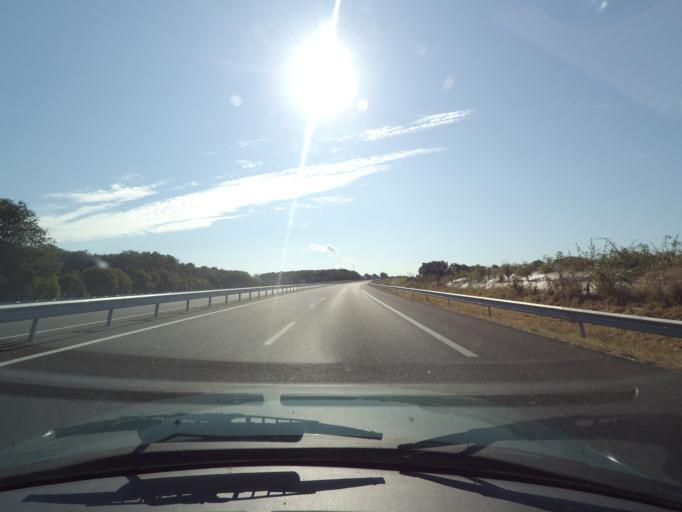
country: FR
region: Poitou-Charentes
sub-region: Departement de la Vienne
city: Terce
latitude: 46.4857
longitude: 0.5253
